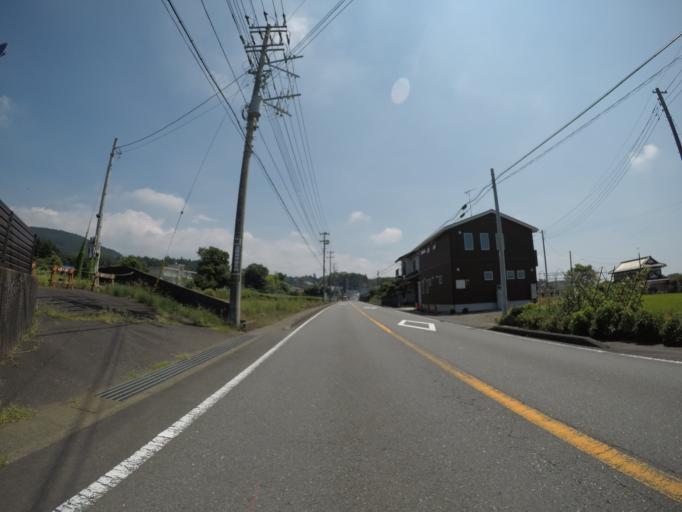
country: JP
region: Shizuoka
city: Fujinomiya
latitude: 35.2694
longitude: 138.6257
